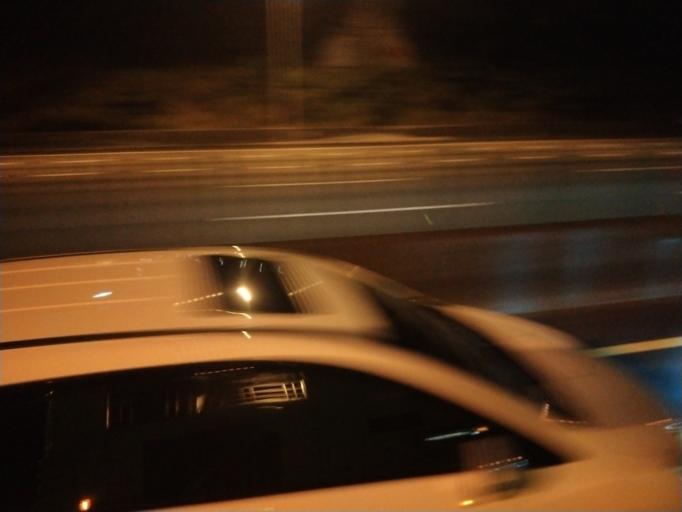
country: TW
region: Taiwan
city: Fengyuan
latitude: 24.3963
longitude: 120.7607
